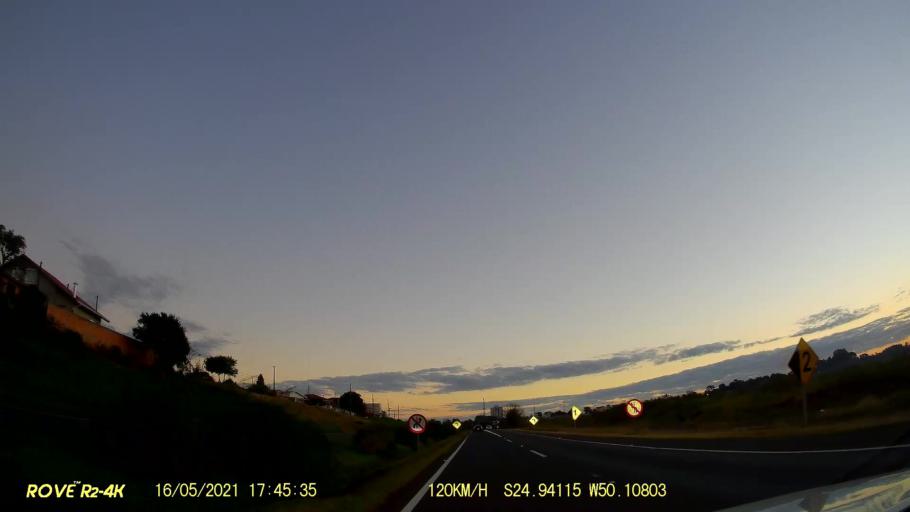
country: BR
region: Parana
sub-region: Carambei
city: Carambei
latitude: -24.9409
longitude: -50.1078
